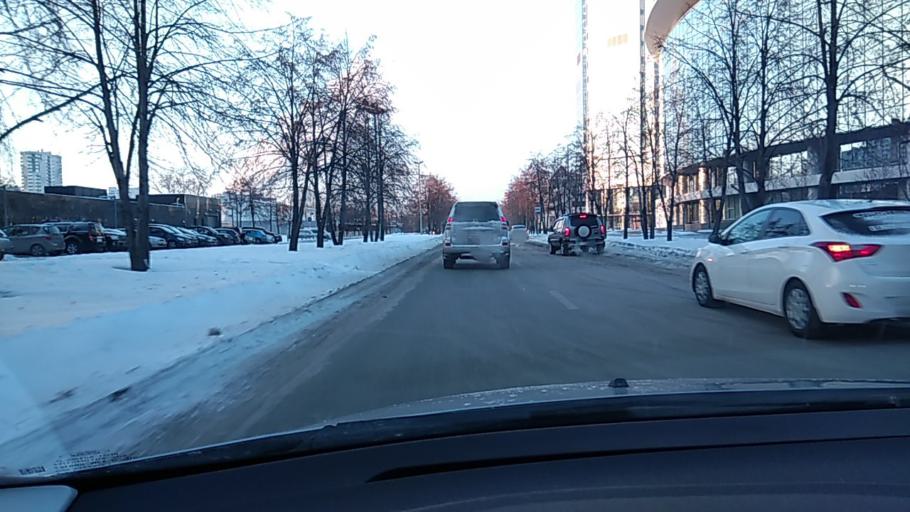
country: RU
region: Sverdlovsk
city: Yekaterinburg
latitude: 56.8437
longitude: 60.5918
